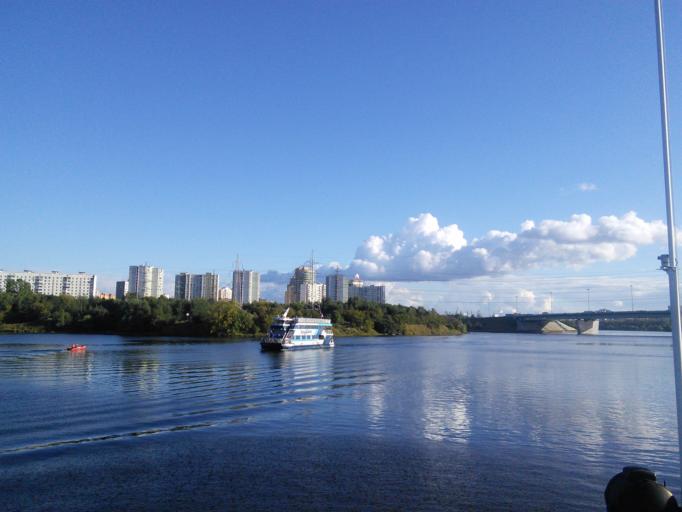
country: RU
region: Moskovskaya
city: Levoberezhnaya
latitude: 55.8783
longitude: 37.4583
